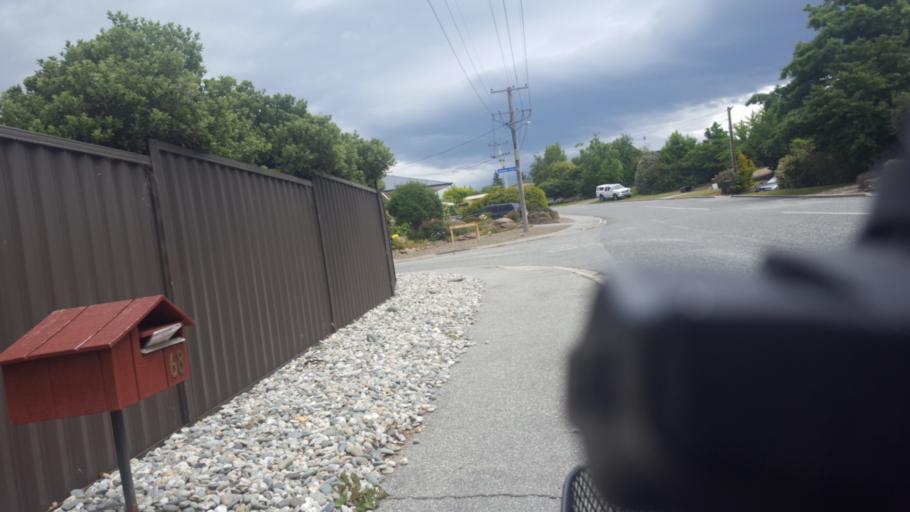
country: NZ
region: Otago
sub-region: Queenstown-Lakes District
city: Wanaka
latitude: -45.2616
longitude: 169.3792
